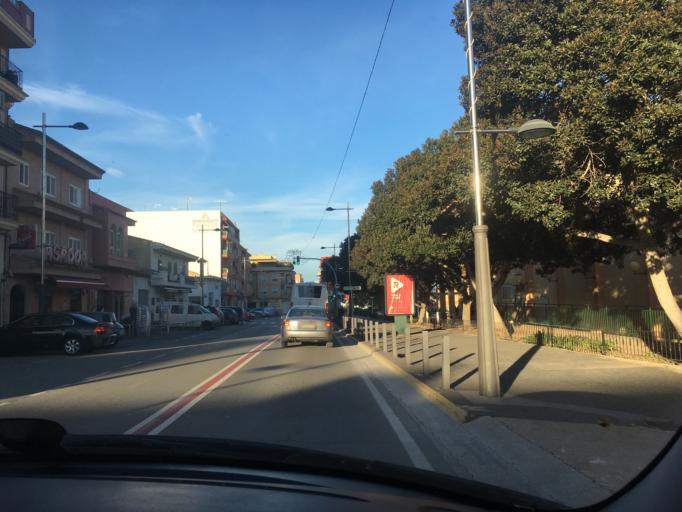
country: ES
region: Valencia
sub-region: Provincia de Valencia
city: Ribarroja
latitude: 39.5405
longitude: -0.5710
